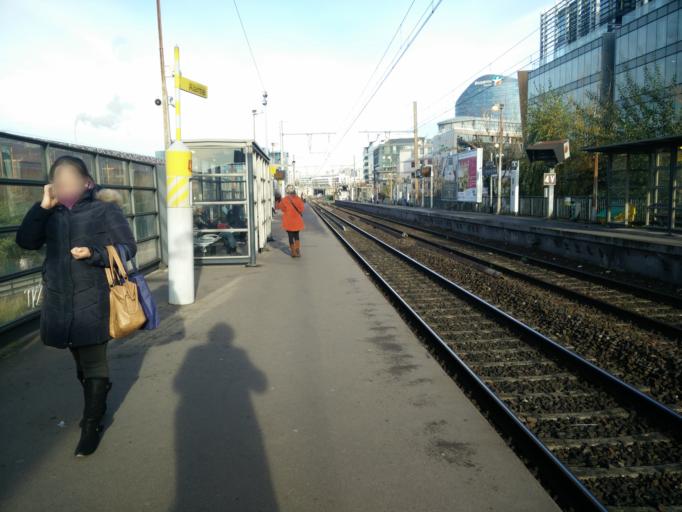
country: FR
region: Ile-de-France
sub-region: Departement des Hauts-de-Seine
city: Boulogne-Billancourt
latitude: 48.8303
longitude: 2.2638
